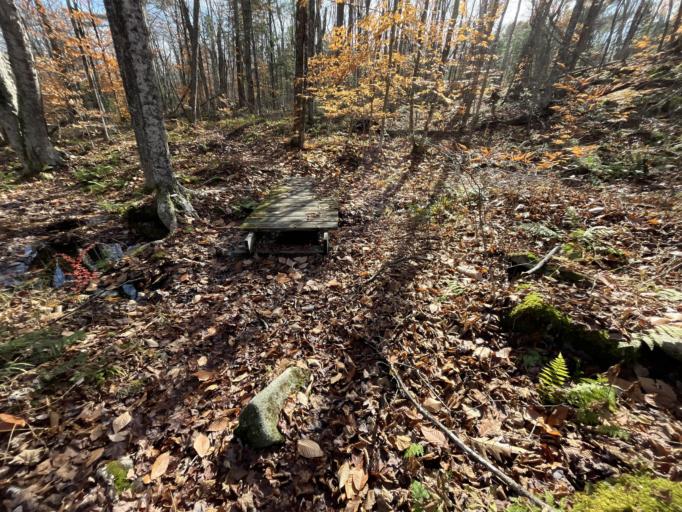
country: US
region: New Hampshire
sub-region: Merrimack County
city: New London
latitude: 43.3972
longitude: -71.9930
